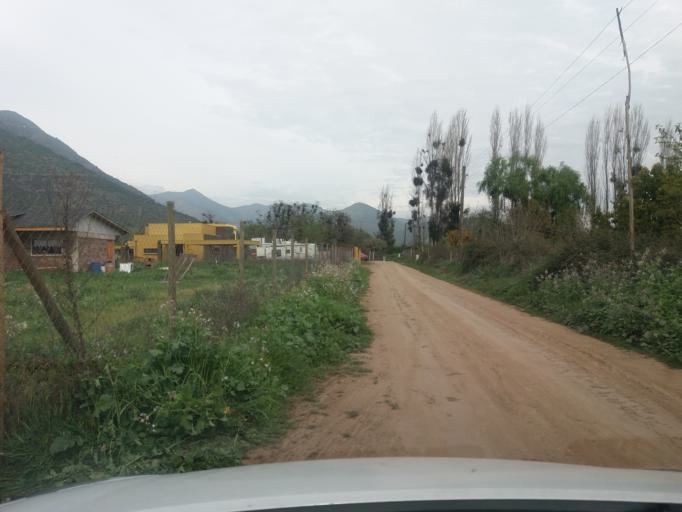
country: CL
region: Valparaiso
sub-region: Provincia de Quillota
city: Hacienda La Calera
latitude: -32.7638
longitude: -71.1677
